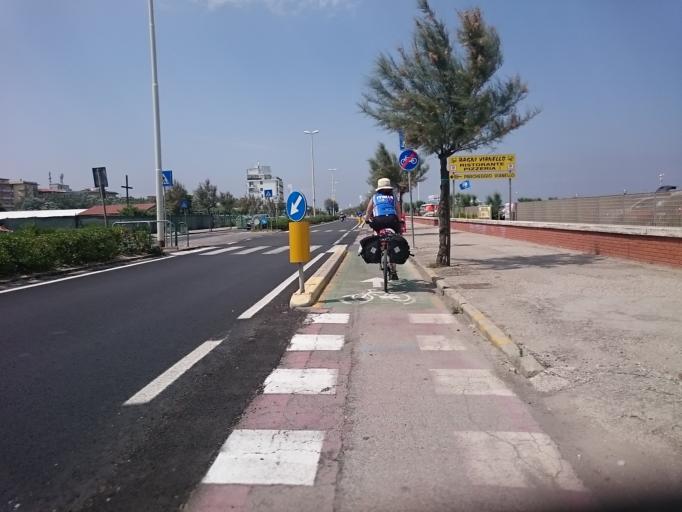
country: IT
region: Veneto
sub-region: Provincia di Venezia
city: Chioggia
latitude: 45.2011
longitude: 12.3008
